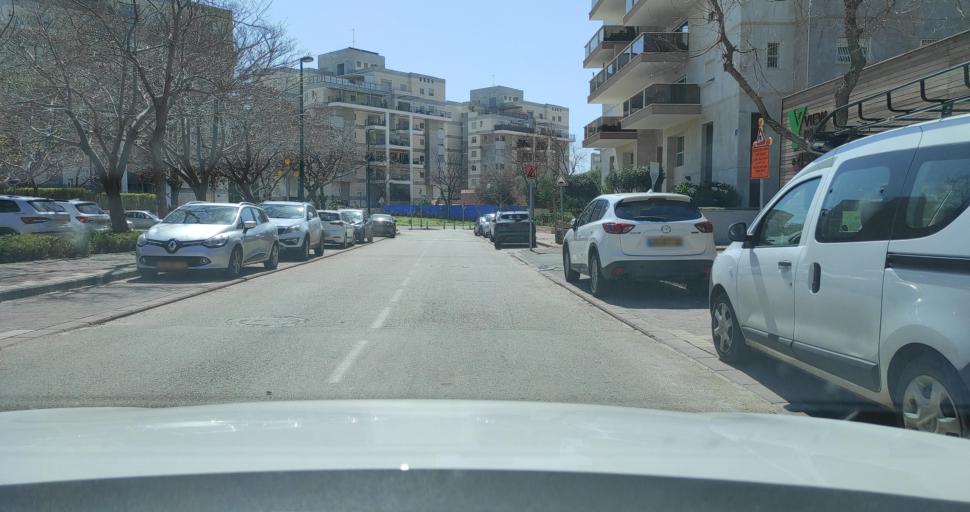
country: IL
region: Central District
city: Nordiyya
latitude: 32.2994
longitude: 34.8757
